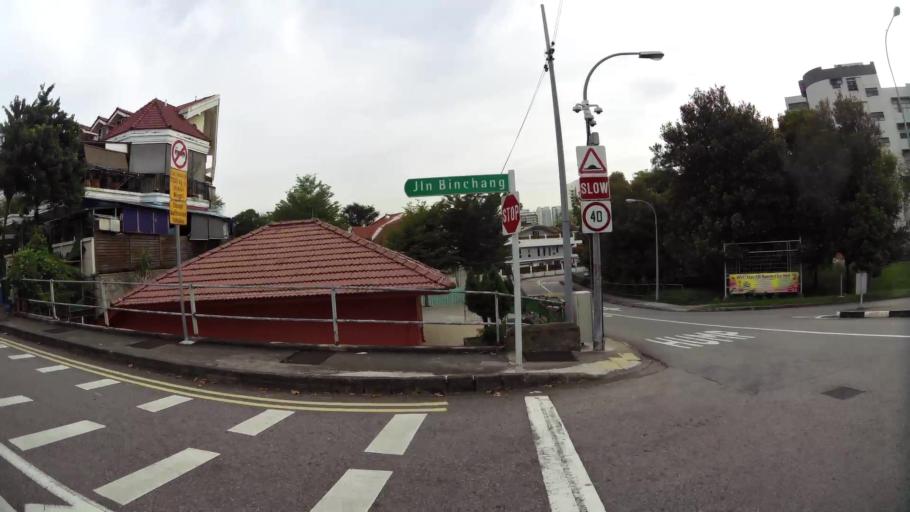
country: SG
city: Singapore
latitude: 1.3521
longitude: 103.8438
